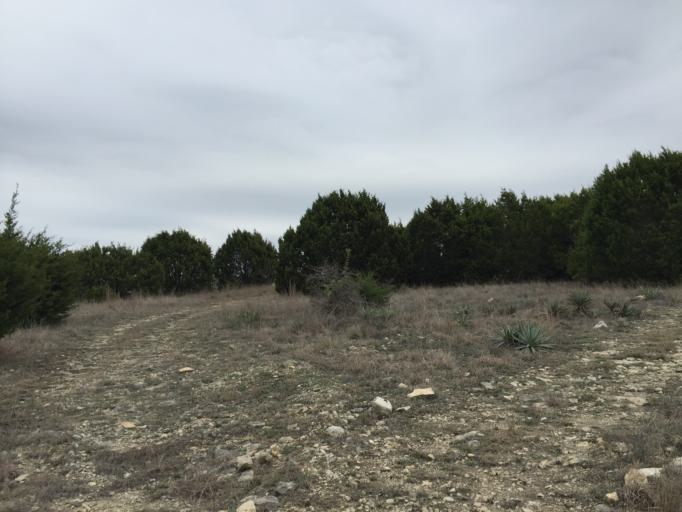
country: US
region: Texas
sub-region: Bell County
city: Fort Hood
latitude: 31.1211
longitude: -97.8161
